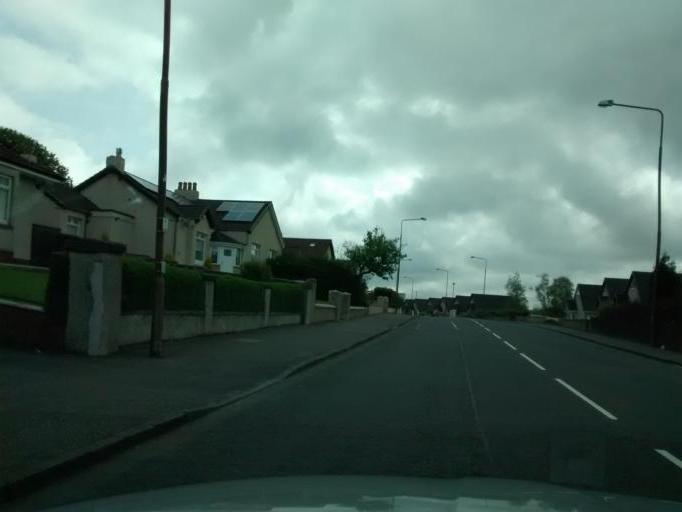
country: GB
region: Scotland
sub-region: North Lanarkshire
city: Harthill
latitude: 55.8842
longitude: -3.7659
